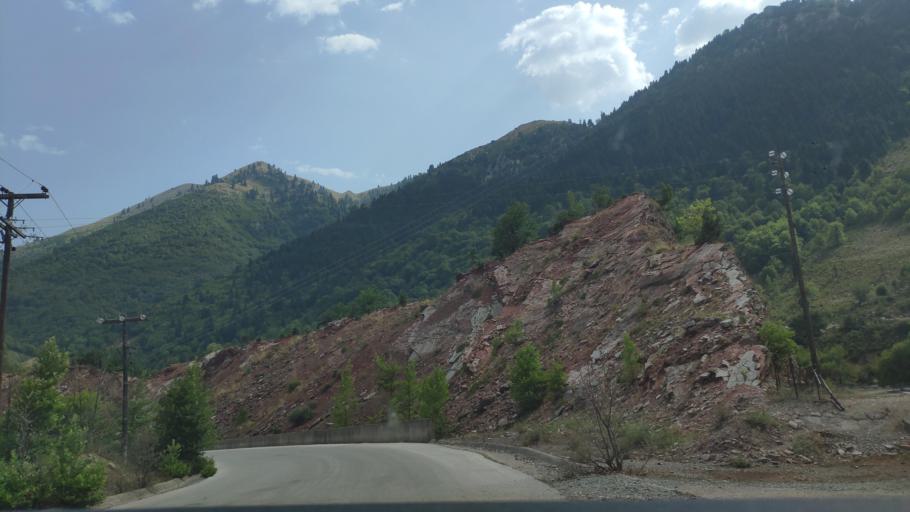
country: GR
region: Epirus
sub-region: Nomos Artas
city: Voulgareli
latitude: 39.4289
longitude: 21.2489
